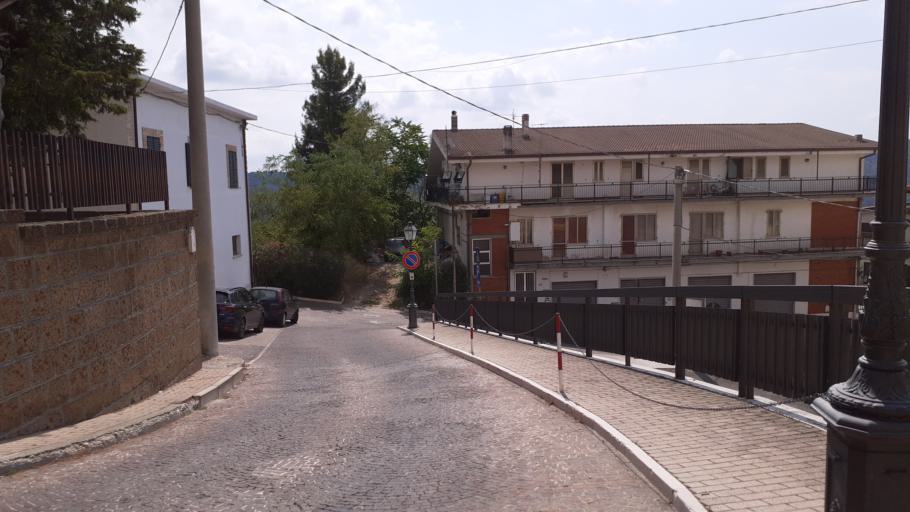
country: IT
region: Abruzzo
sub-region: Provincia di Chieti
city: Vacri
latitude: 42.2956
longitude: 14.2297
